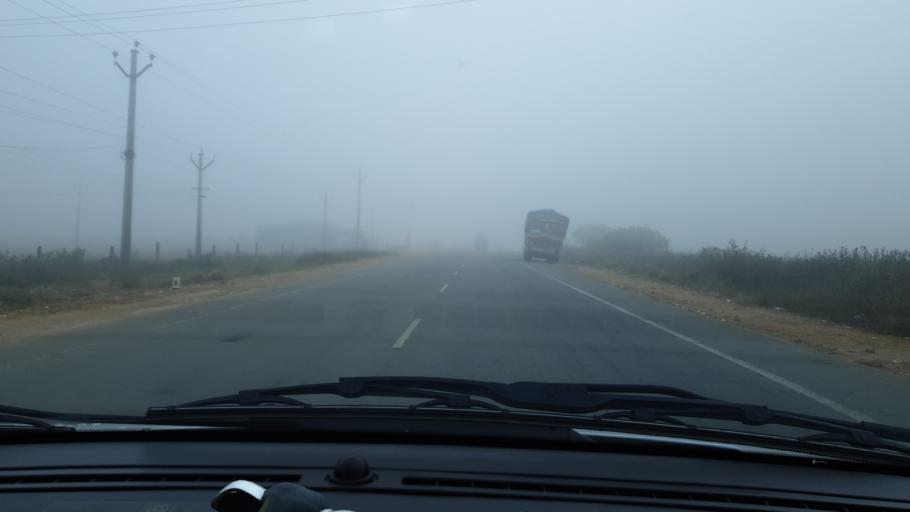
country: IN
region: Telangana
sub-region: Mahbubnagar
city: Nagar Karnul
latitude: 16.6625
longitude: 78.5370
